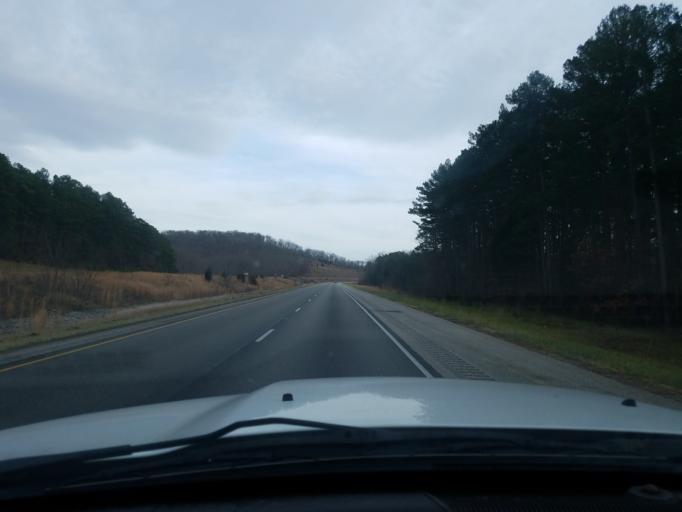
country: US
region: Indiana
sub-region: Crawford County
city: English
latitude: 38.2377
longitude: -86.5227
